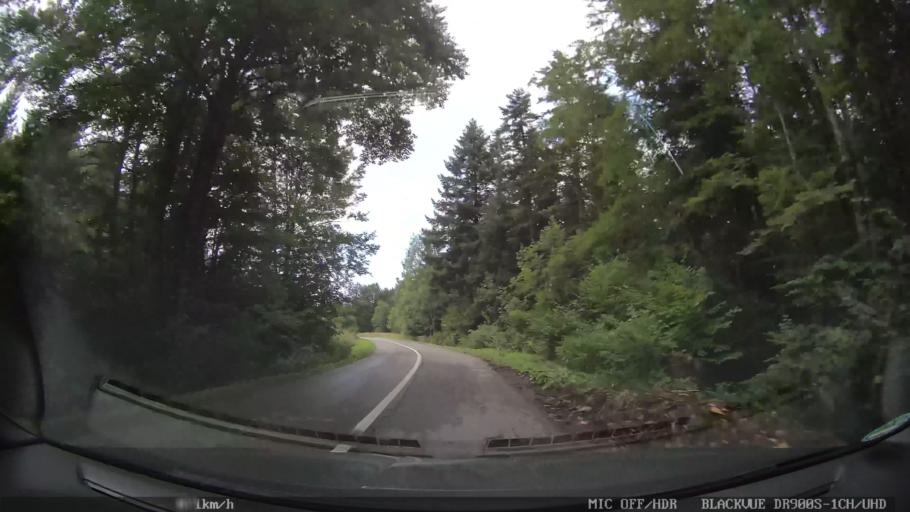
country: HR
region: Licko-Senjska
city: Jezerce
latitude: 44.9562
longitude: 15.5269
